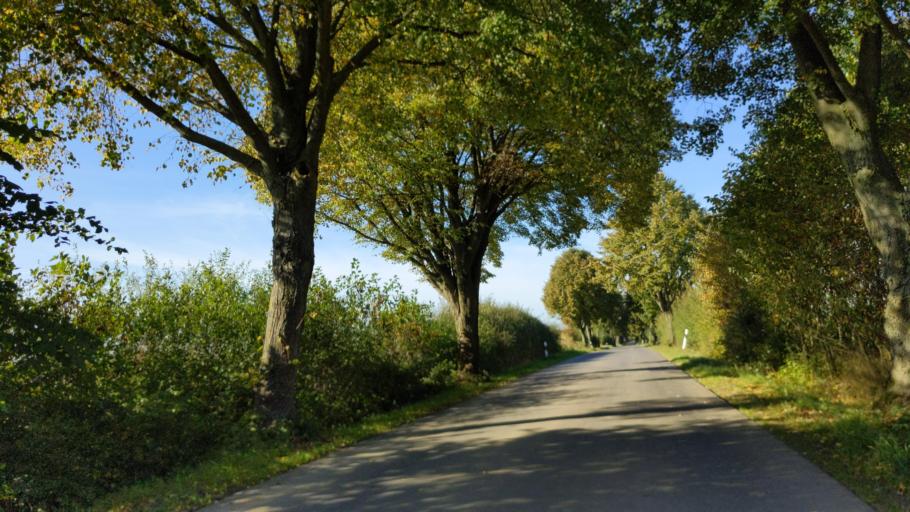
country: DE
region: Schleswig-Holstein
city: Ahrensbok
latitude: 54.0283
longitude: 10.6149
